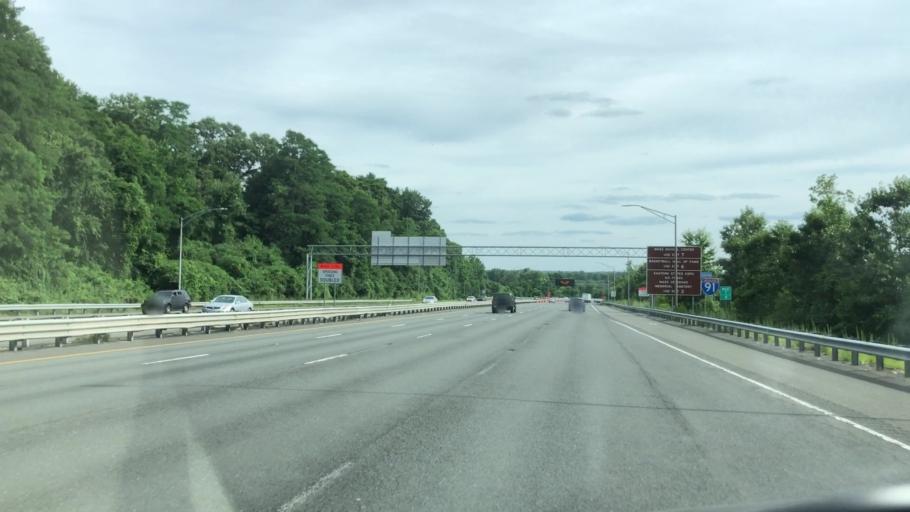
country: US
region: Massachusetts
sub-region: Hampden County
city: Chicopee
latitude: 42.1273
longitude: -72.6085
